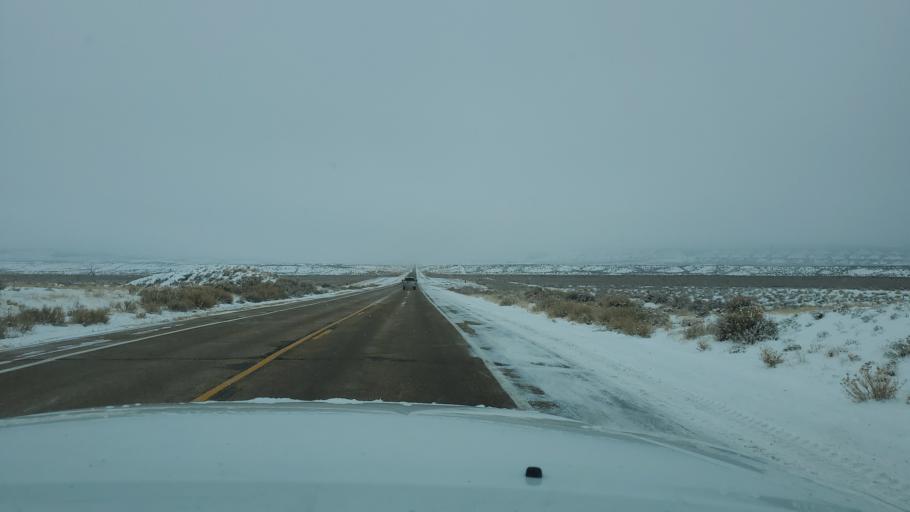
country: US
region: Colorado
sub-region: Rio Blanco County
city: Rangely
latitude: 40.2562
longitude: -108.6746
